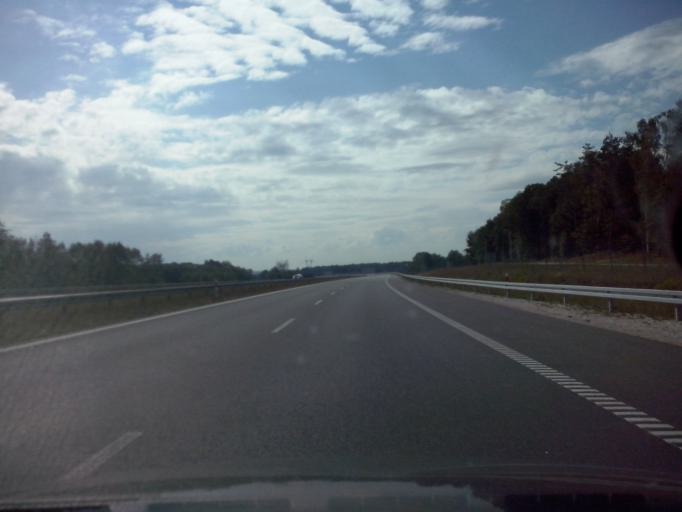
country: PL
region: Lesser Poland Voivodeship
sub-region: Powiat tarnowski
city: Jodlowka-Walki
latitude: 50.0870
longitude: 21.1469
